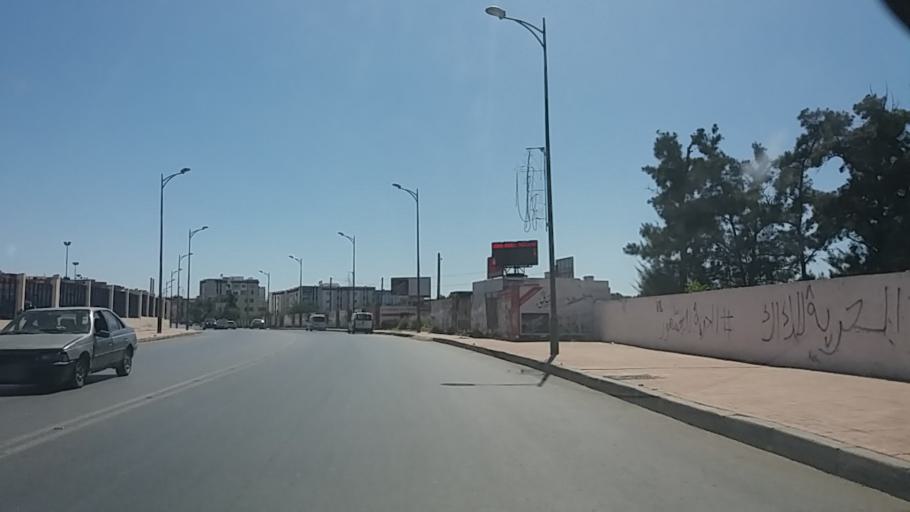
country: MA
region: Gharb-Chrarda-Beni Hssen
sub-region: Kenitra Province
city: Kenitra
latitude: 34.2485
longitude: -6.6093
